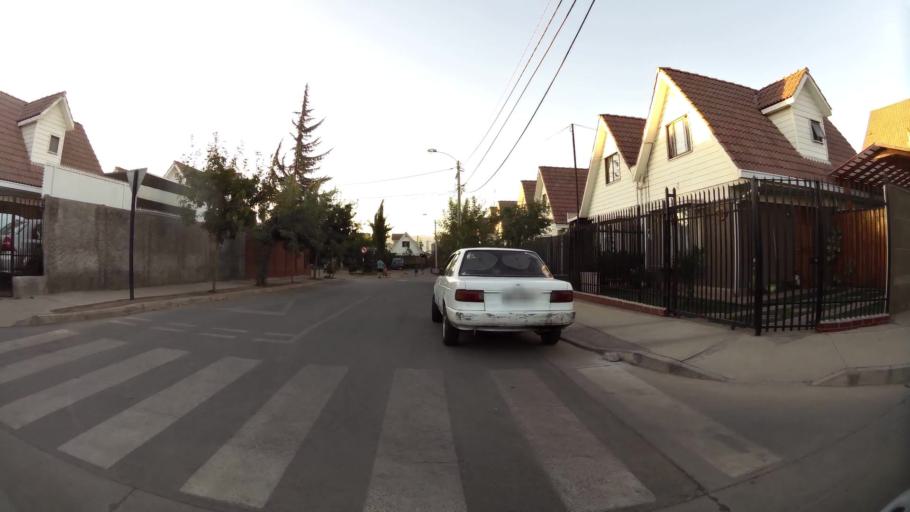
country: CL
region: O'Higgins
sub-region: Provincia de Cachapoal
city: Rancagua
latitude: -34.1905
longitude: -70.7411
